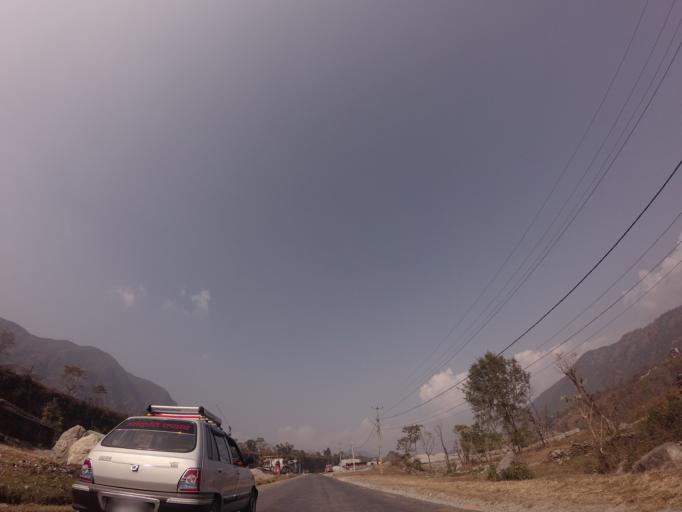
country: NP
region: Western Region
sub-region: Gandaki Zone
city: Pokhara
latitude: 28.2583
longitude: 83.9618
